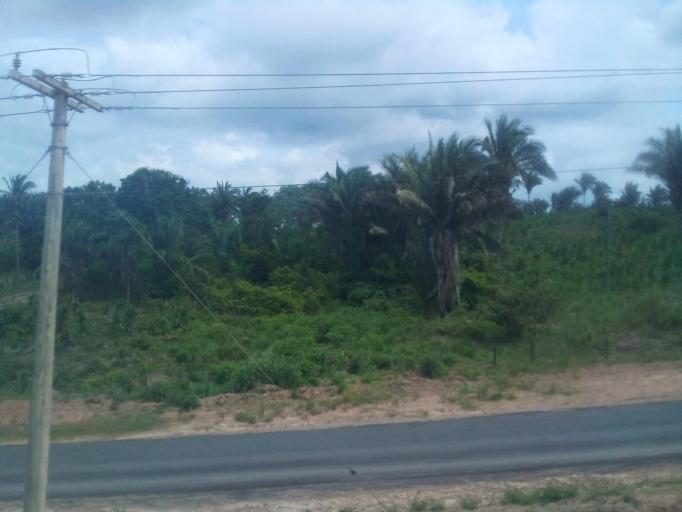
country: BR
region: Maranhao
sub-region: Santa Ines
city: Santa Ines
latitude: -3.7078
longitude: -46.0078
